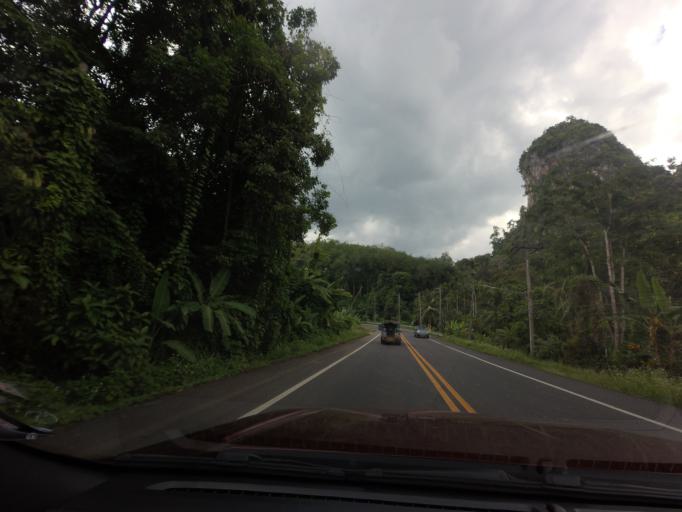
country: TH
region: Yala
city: Than To
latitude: 6.2086
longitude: 101.1687
